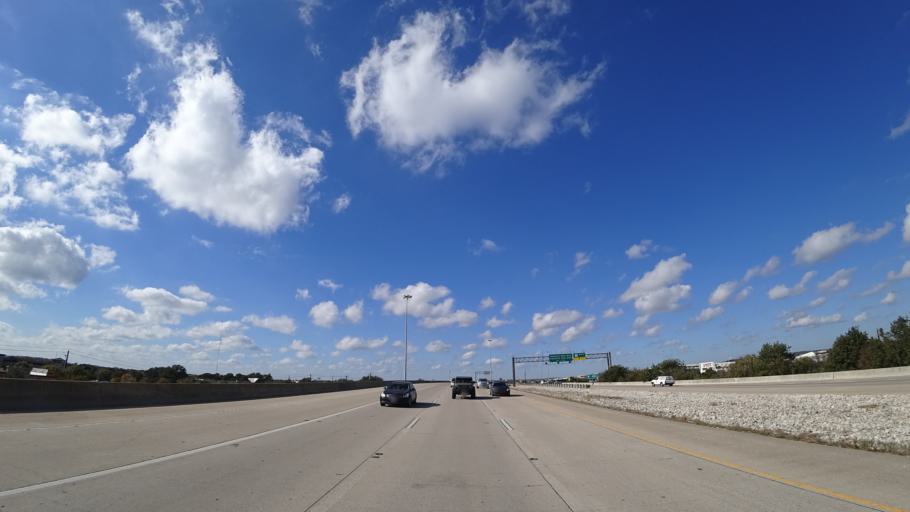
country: US
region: Texas
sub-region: Travis County
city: Rollingwood
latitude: 30.2331
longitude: -97.8162
